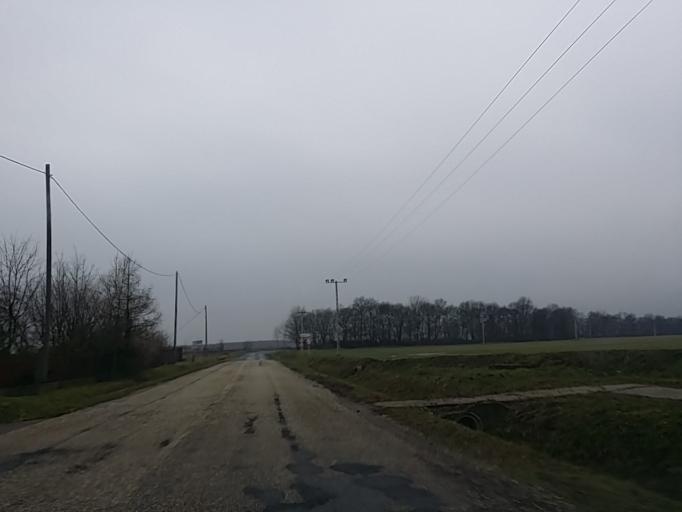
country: HU
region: Borsod-Abauj-Zemplen
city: Saly
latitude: 47.8907
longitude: 20.6752
